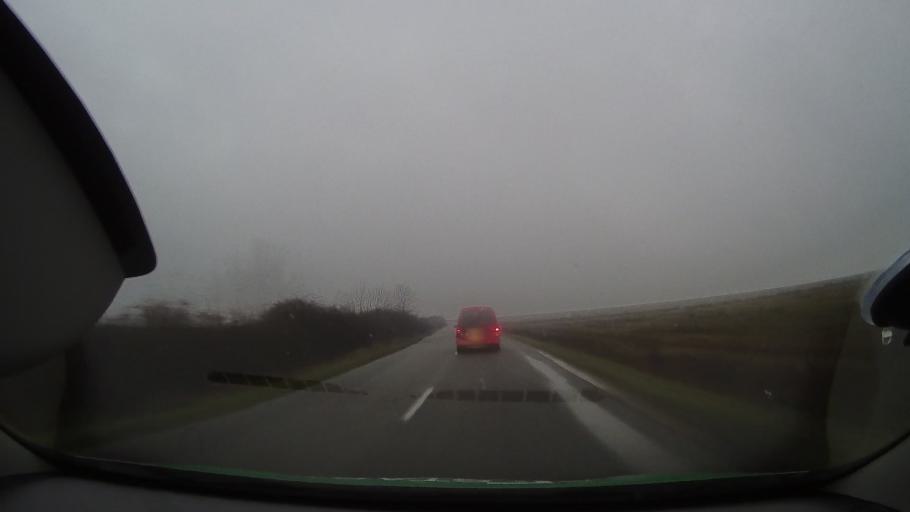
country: RO
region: Arad
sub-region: Comuna Craiova
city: Craiova
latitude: 46.6135
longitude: 21.9566
